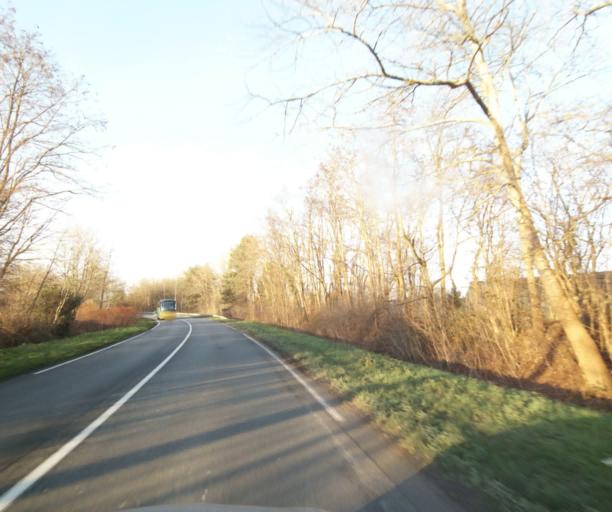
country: FR
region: Nord-Pas-de-Calais
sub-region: Departement du Nord
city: Famars
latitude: 50.3271
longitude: 3.5178
